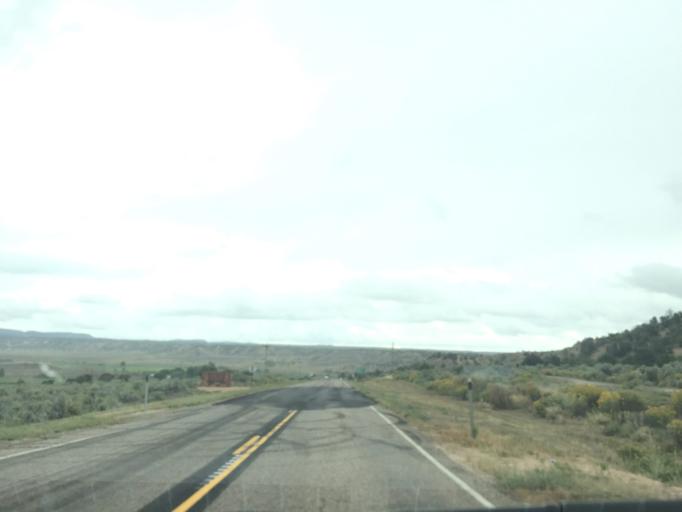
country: US
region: Utah
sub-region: Garfield County
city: Panguitch
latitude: 37.6139
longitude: -112.0723
